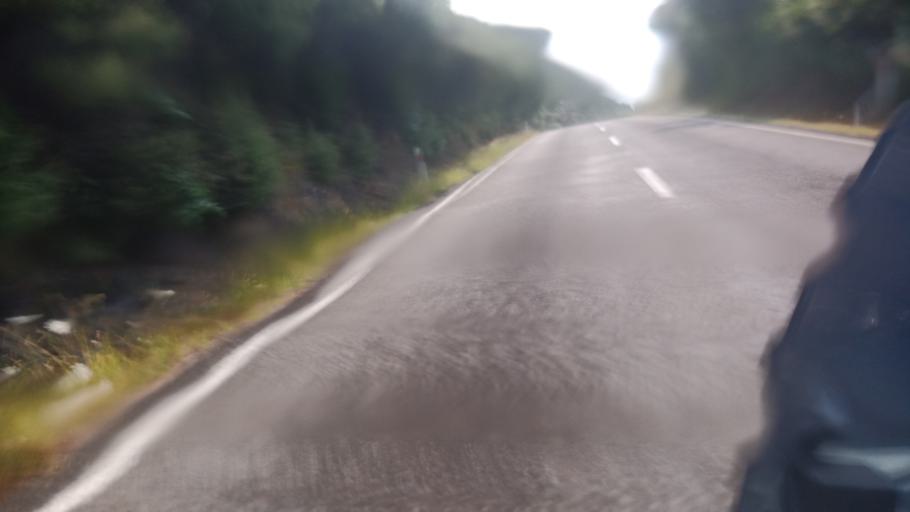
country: NZ
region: Bay of Plenty
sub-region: Opotiki District
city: Opotiki
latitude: -37.6641
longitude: 177.8315
